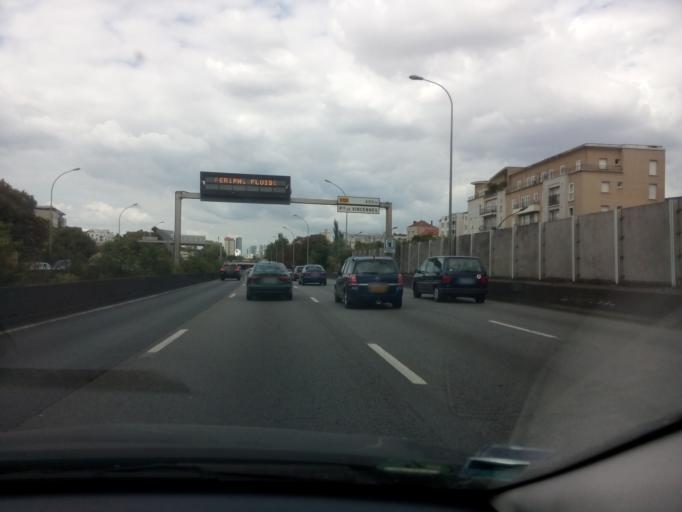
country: FR
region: Ile-de-France
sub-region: Departement du Val-de-Marne
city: Saint-Mande
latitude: 48.8403
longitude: 2.4137
